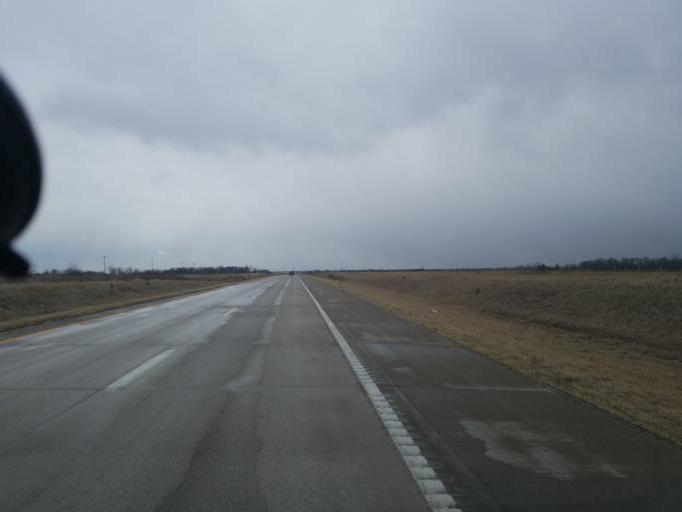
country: US
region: Missouri
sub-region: Randolph County
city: Moberly
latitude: 39.4875
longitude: -92.4344
